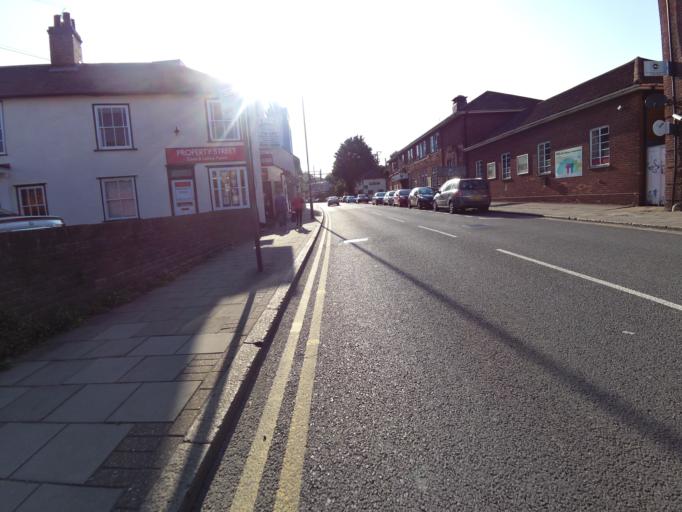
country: GB
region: England
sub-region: Essex
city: Chelmsford
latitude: 51.7371
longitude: 0.4729
